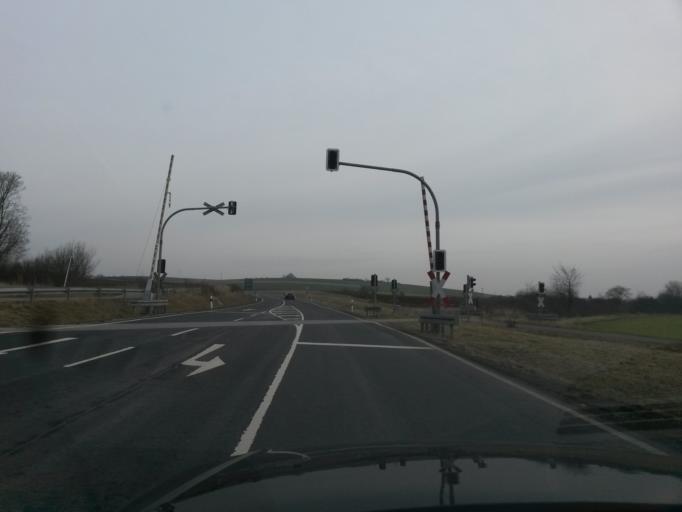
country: DE
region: Bavaria
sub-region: Regierungsbezirk Unterfranken
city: Stockheim
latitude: 50.4486
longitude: 10.2914
